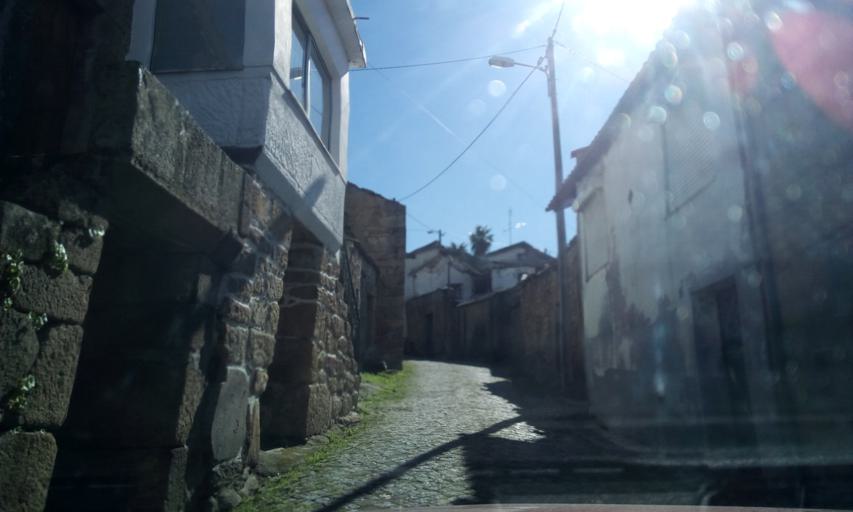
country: PT
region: Guarda
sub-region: Guarda
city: Guarda
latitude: 40.5860
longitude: -7.2881
